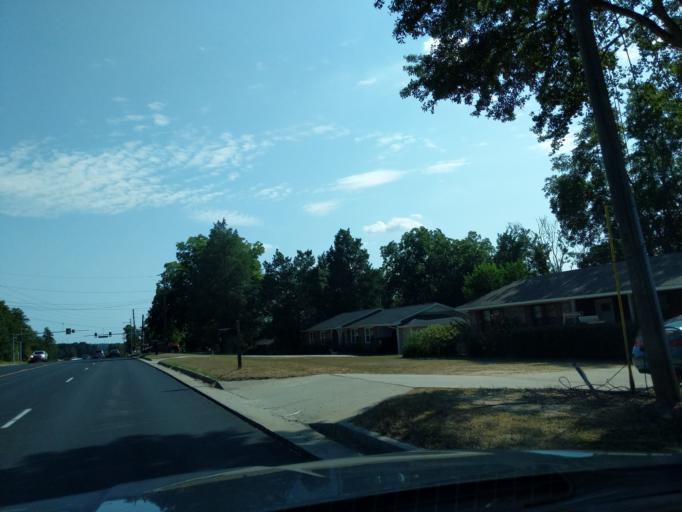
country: US
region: Georgia
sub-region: Columbia County
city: Evans
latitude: 33.4989
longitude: -82.1393
